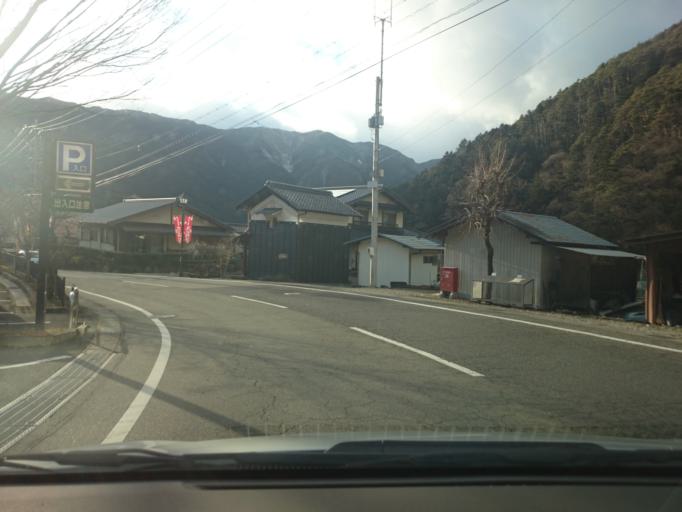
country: JP
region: Gifu
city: Gujo
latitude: 35.8099
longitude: 137.2503
